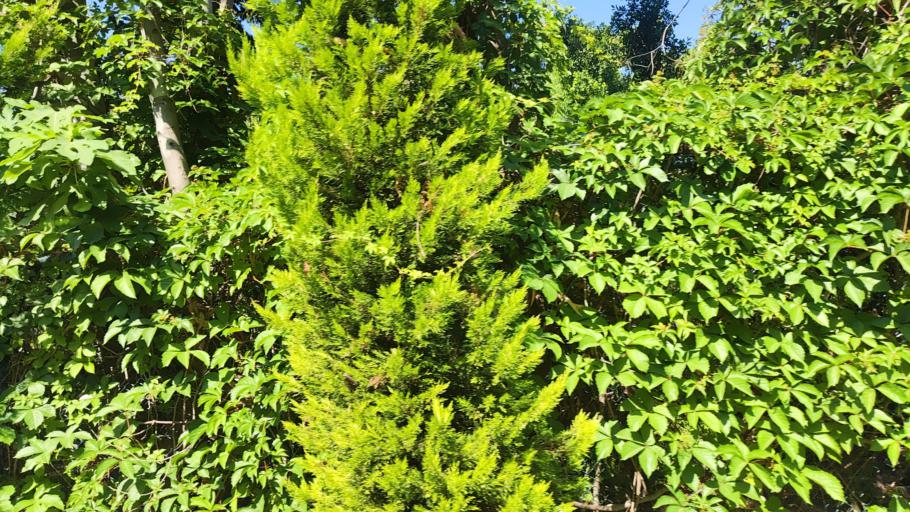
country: TR
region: Mugla
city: Sarigerme
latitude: 36.7024
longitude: 28.6950
